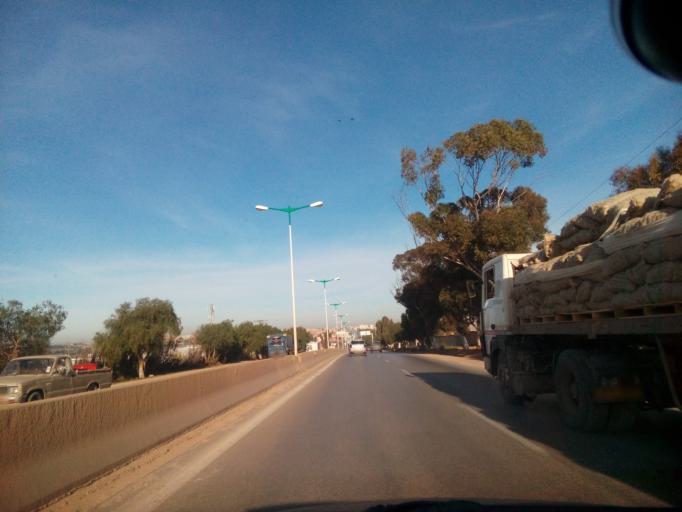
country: DZ
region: Mostaganem
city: Mostaganem
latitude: 35.8979
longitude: 0.1246
